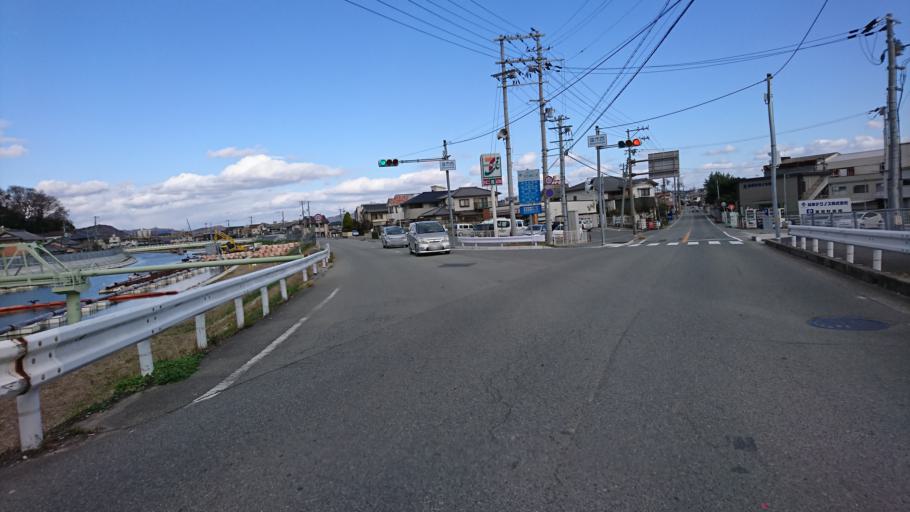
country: JP
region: Hyogo
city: Kakogawacho-honmachi
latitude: 34.7742
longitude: 134.7993
